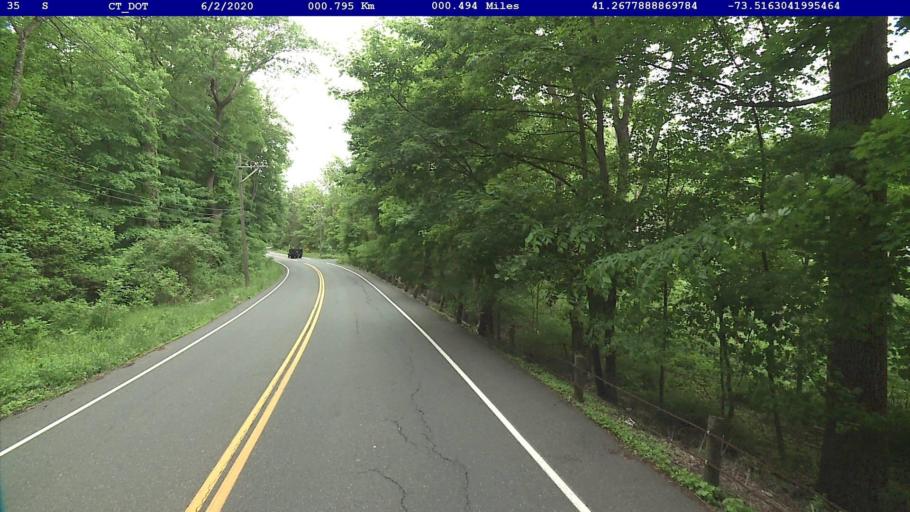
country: US
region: Connecticut
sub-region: Fairfield County
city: Ridgefield
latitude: 41.2677
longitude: -73.5162
